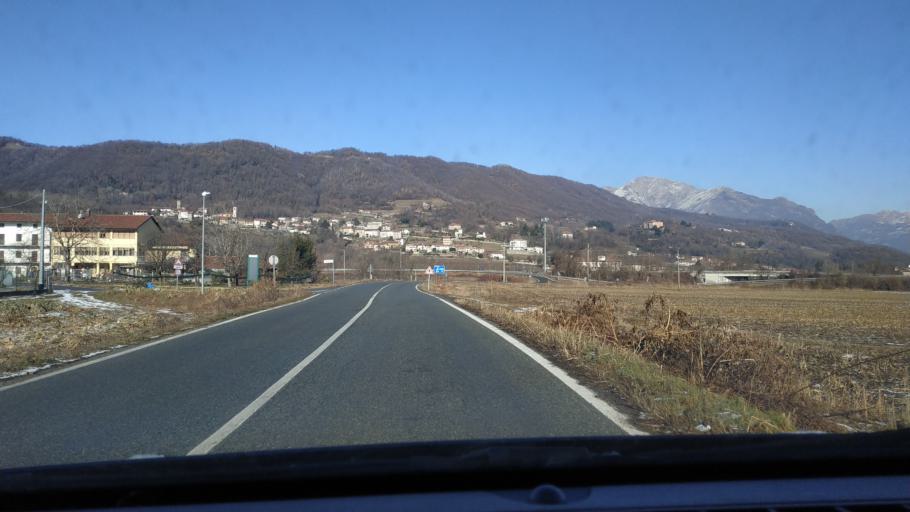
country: IT
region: Piedmont
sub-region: Provincia di Torino
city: Colleretto Giacosa
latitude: 45.4219
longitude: 7.7986
